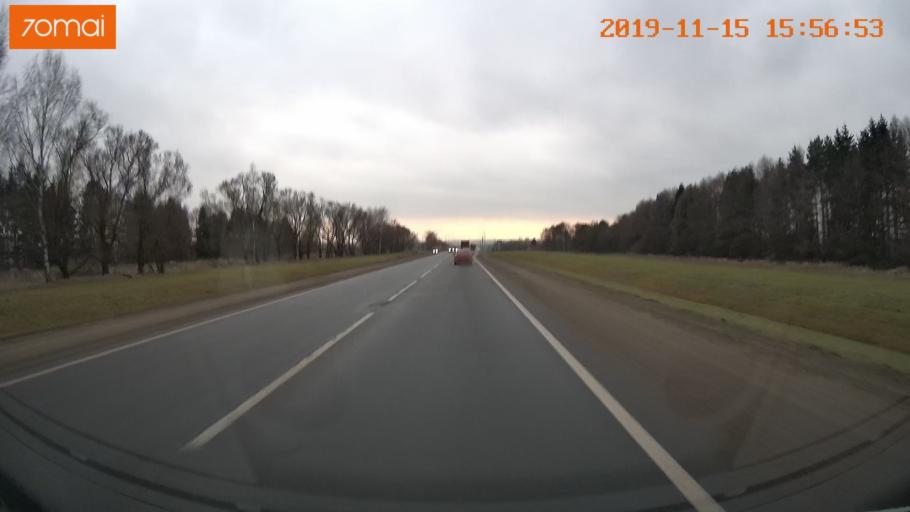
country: RU
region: Jaroslavl
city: Yaroslavl
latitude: 57.8369
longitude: 39.9690
